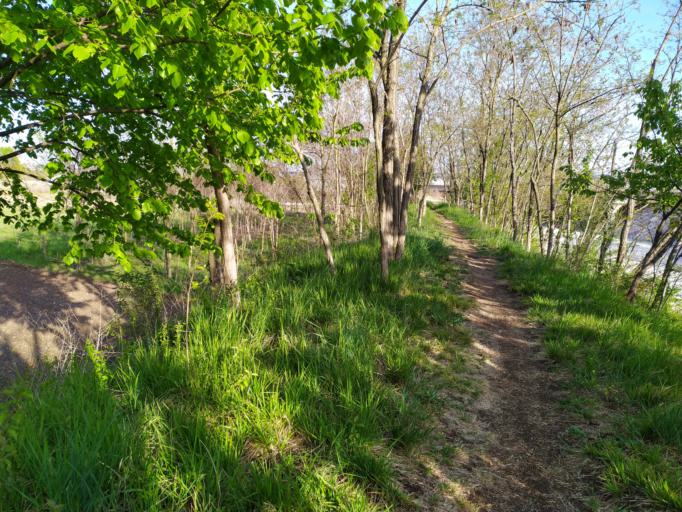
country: IT
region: Veneto
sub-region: Provincia di Vicenza
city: Isola Vicentina
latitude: 45.6505
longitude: 11.4572
